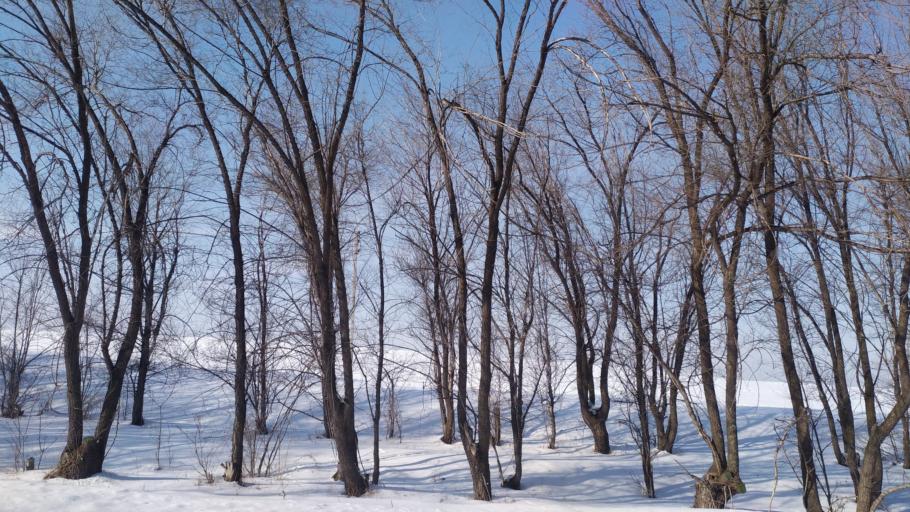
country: KZ
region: Almaty Oblysy
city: Burunday
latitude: 43.2571
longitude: 76.4669
